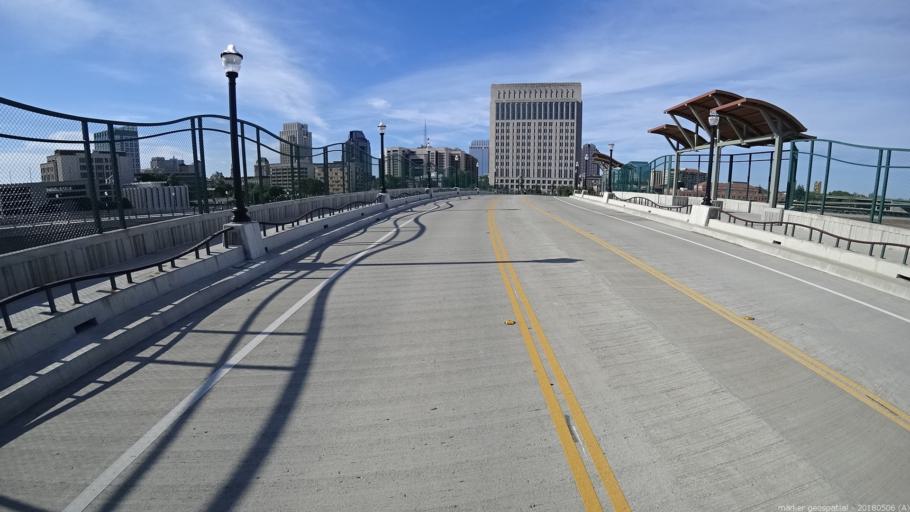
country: US
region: California
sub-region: Sacramento County
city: Sacramento
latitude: 38.5866
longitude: -121.4975
